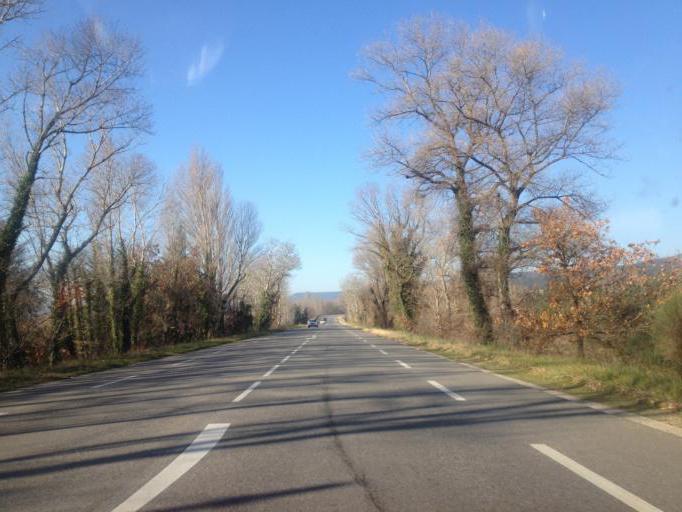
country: FR
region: Rhone-Alpes
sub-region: Departement de la Drome
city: Donzere
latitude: 44.4348
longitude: 4.6894
